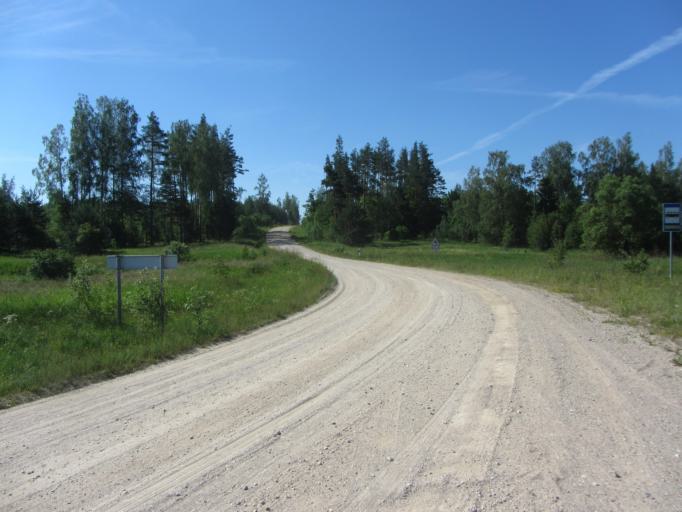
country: LT
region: Alytaus apskritis
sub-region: Alytaus rajonas
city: Daugai
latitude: 54.4318
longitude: 24.4584
